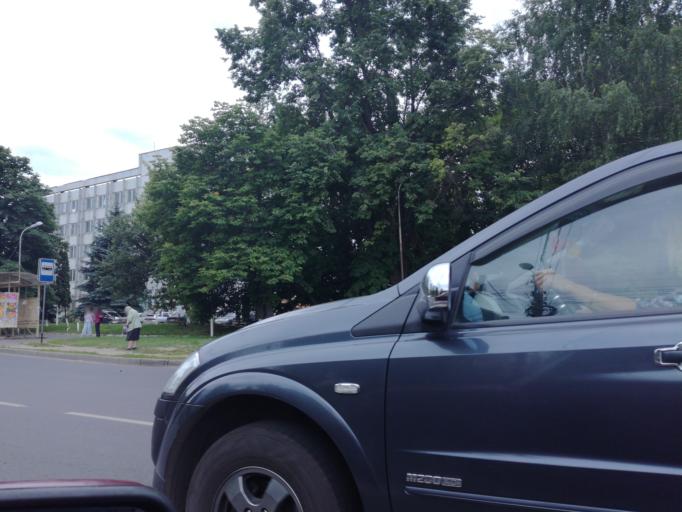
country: RU
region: Kursk
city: Kursk
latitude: 51.7276
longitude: 36.1595
